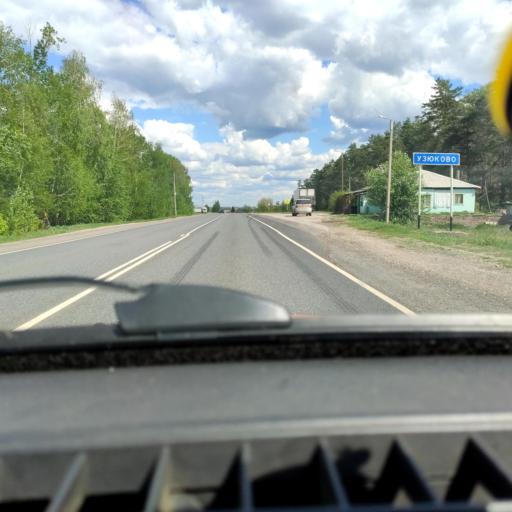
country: RU
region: Samara
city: Povolzhskiy
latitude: 53.6283
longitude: 49.6560
